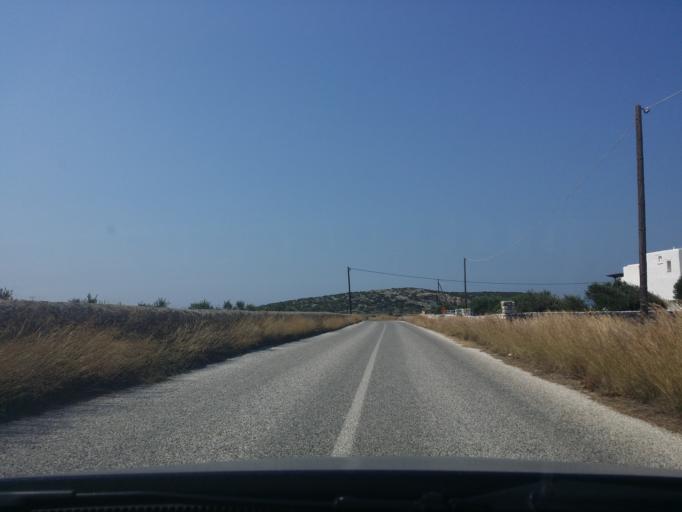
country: GR
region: South Aegean
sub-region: Nomos Kykladon
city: Antiparos
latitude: 37.0192
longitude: 25.1110
